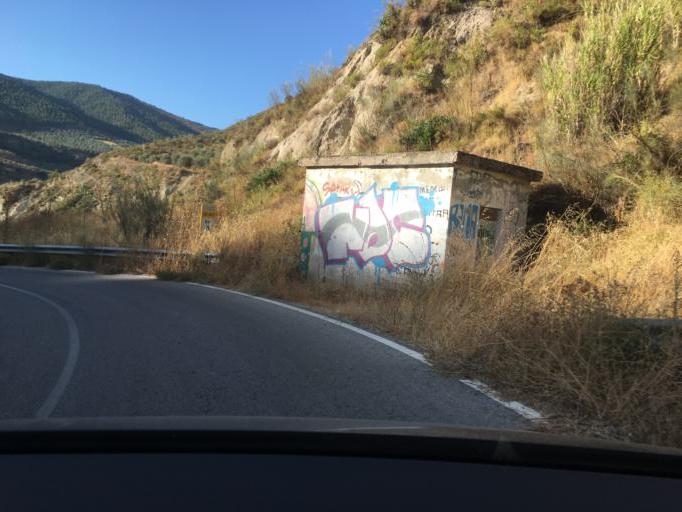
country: ES
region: Andalusia
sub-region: Provincia de Granada
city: Quentar
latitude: 37.1971
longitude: -3.4730
